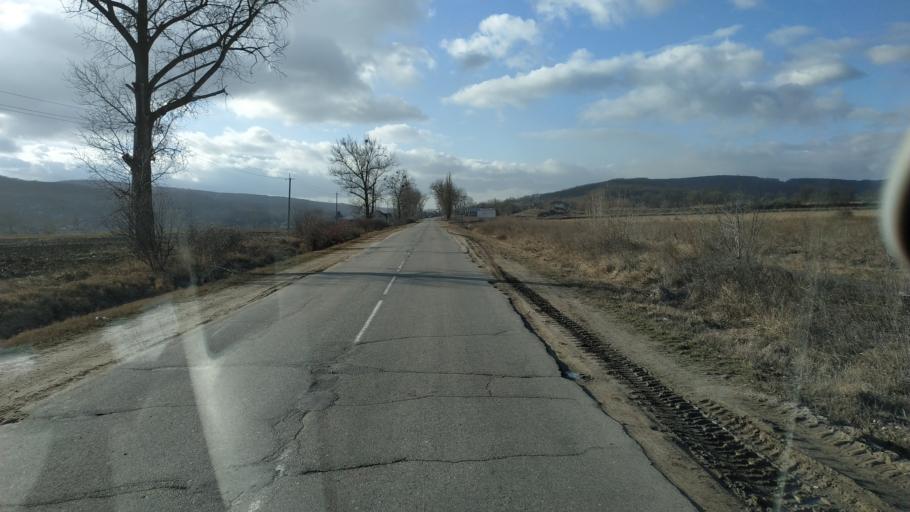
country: MD
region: Calarasi
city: Calarasi
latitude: 47.3273
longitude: 28.0990
